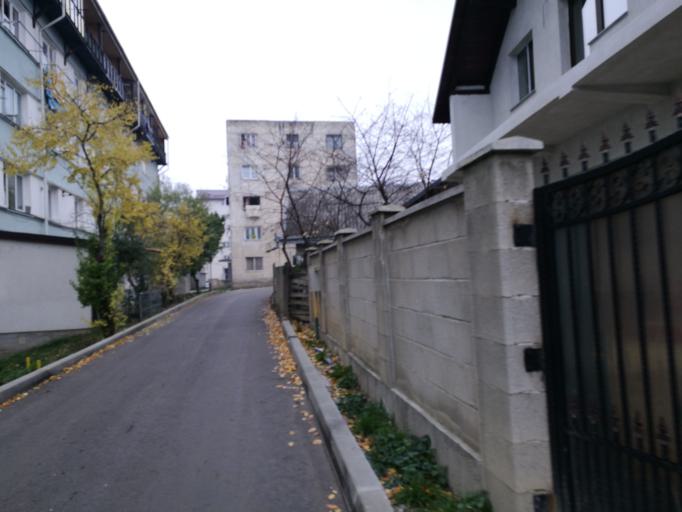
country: RO
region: Suceava
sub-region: Comuna Scheia
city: Scheia
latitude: 47.6714
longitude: 26.2684
